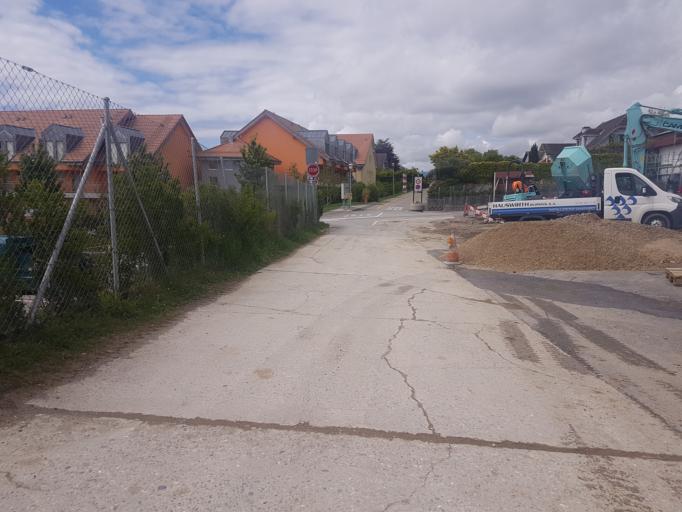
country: CH
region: Vaud
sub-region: Nyon District
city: Rolle
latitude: 46.4669
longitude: 6.3458
